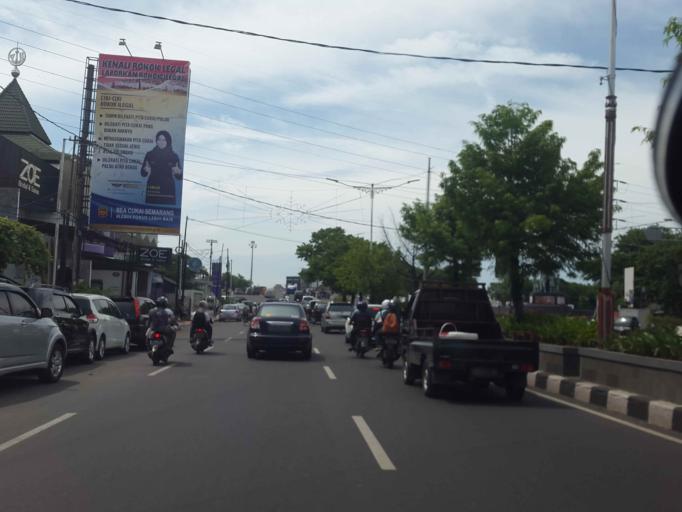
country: ID
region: Central Java
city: Semarang
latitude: -6.9818
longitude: 110.4036
